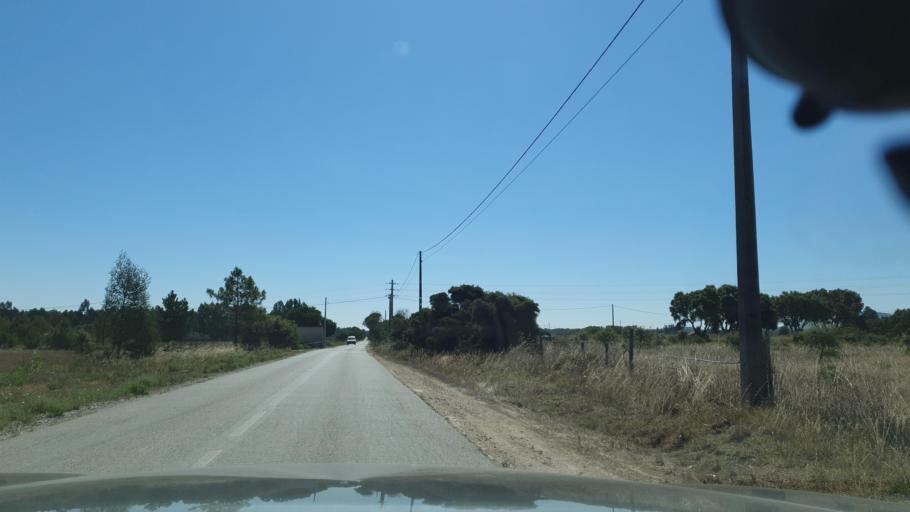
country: PT
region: Beja
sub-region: Odemira
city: Sao Teotonio
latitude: 37.5014
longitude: -8.6858
